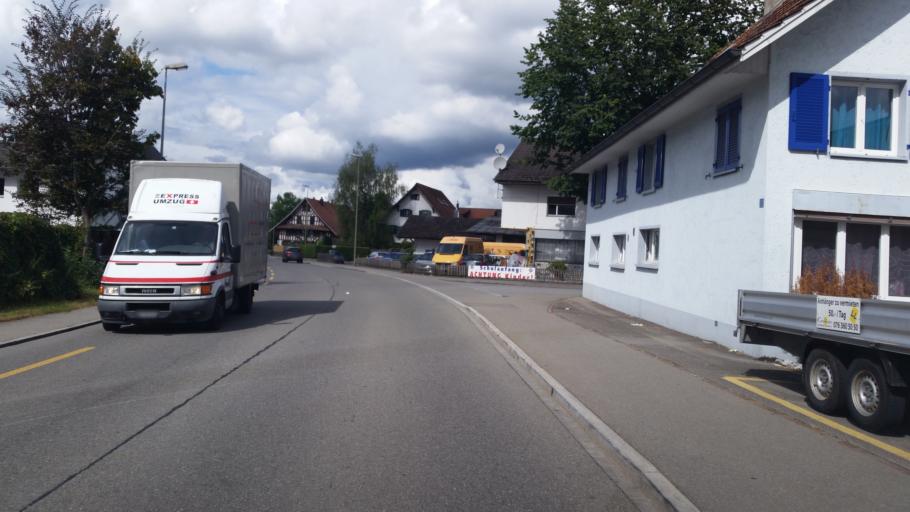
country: CH
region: Zurich
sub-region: Bezirk Affoltern
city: Ottenbach
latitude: 47.2778
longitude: 8.4074
